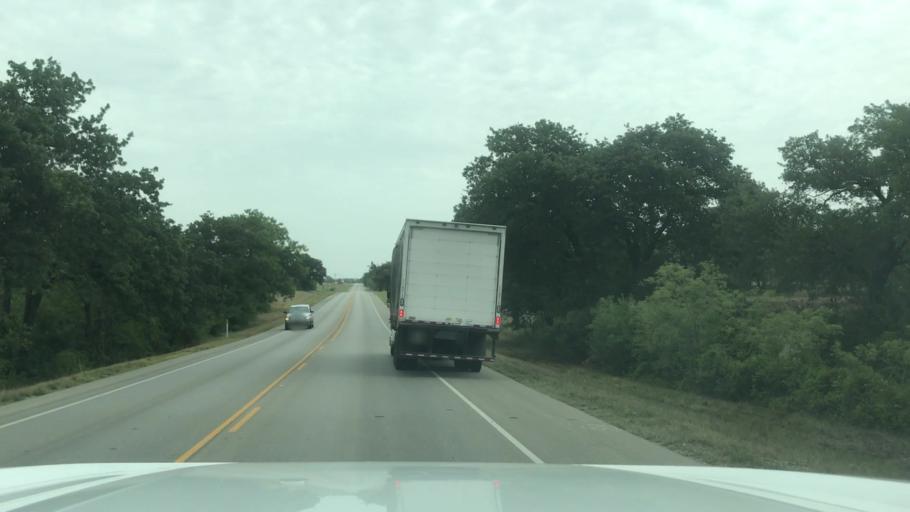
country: US
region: Texas
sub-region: Erath County
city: Dublin
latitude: 32.0901
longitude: -98.4232
